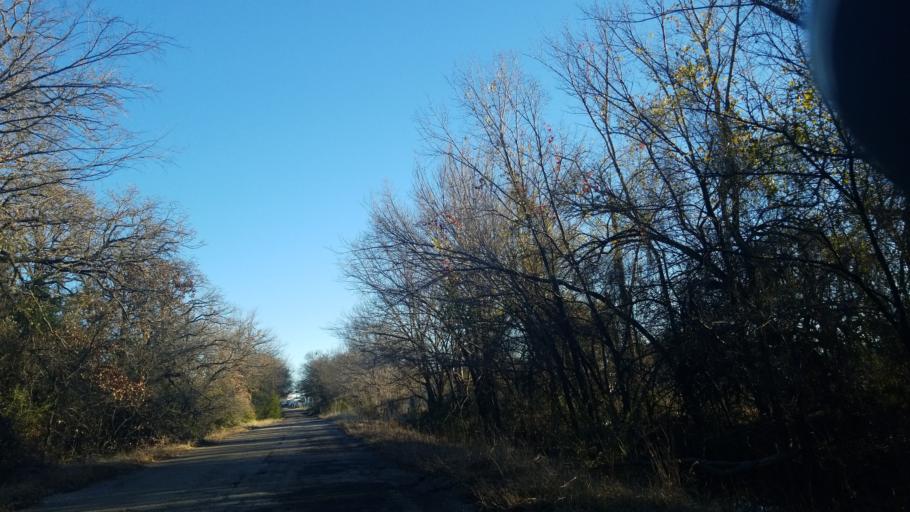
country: US
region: Texas
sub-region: Denton County
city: Corinth
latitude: 33.1614
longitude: -97.0675
